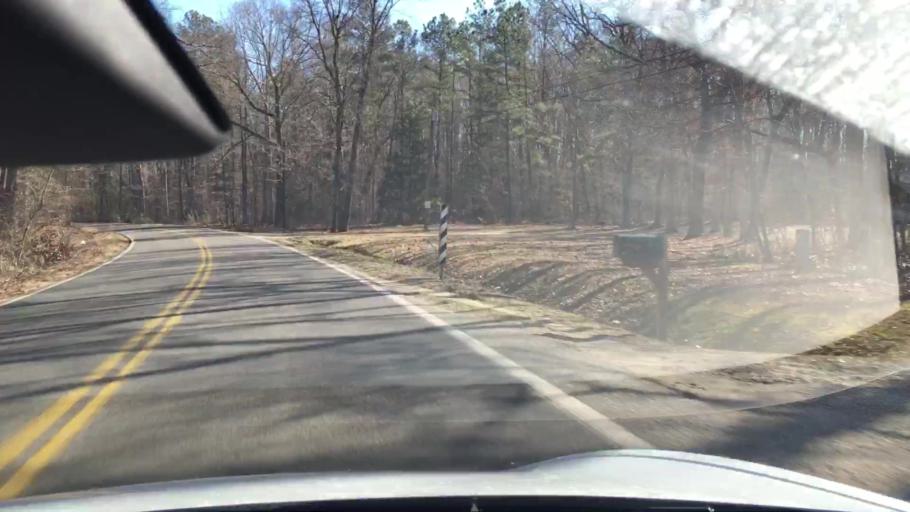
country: US
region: Virginia
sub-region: Henrico County
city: Short Pump
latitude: 37.5786
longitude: -77.7355
